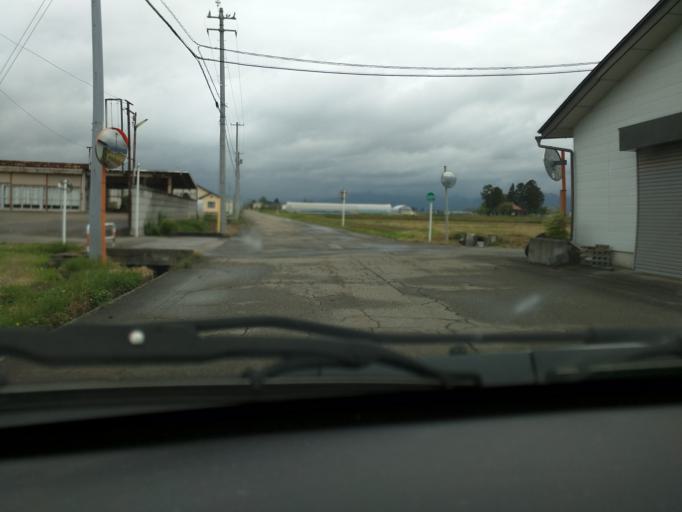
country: JP
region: Fukushima
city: Kitakata
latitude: 37.6085
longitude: 139.8691
